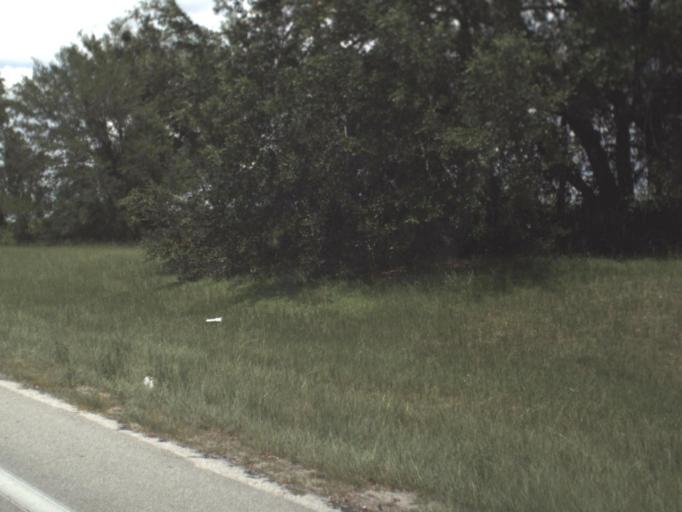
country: US
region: Florida
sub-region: Alachua County
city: Newberry
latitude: 29.6662
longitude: -82.6069
